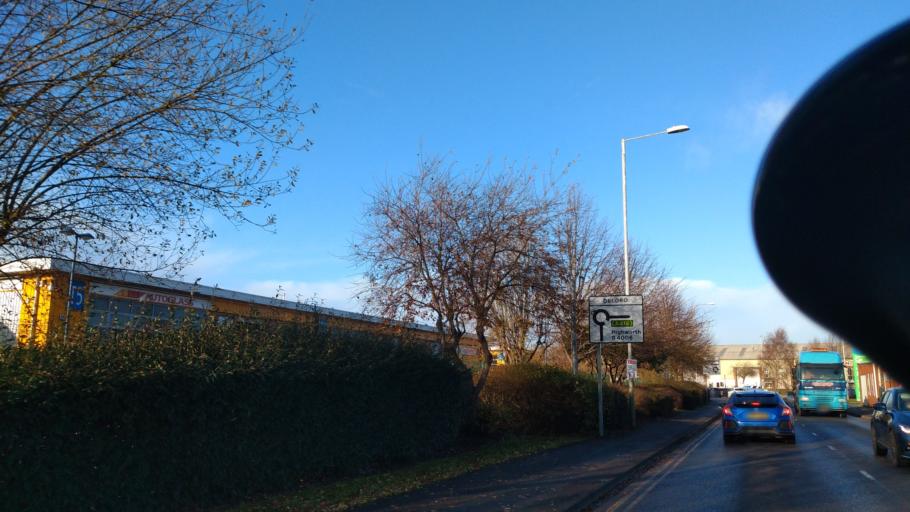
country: GB
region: England
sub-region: Borough of Swindon
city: Swindon
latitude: 51.5823
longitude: -1.7512
